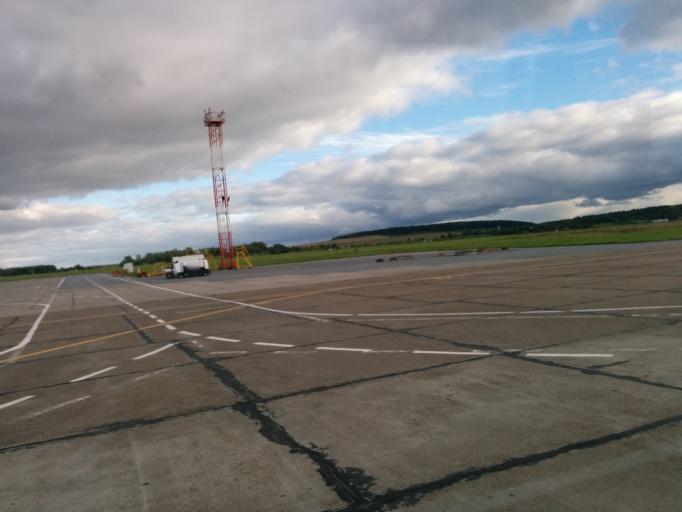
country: RU
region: Perm
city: Kultayevo
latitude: 57.9181
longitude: 56.0201
